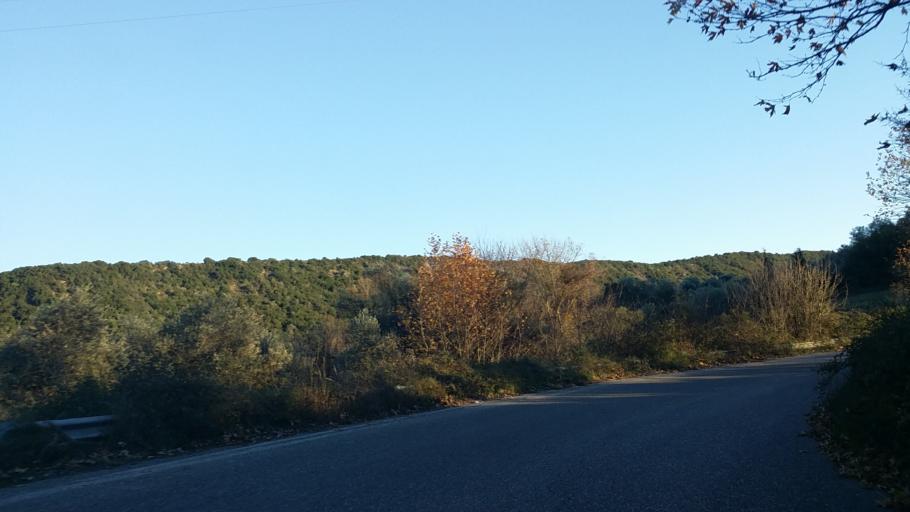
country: GR
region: West Greece
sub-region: Nomos Aitolias kai Akarnanias
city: Neapolis
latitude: 38.7100
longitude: 21.3490
